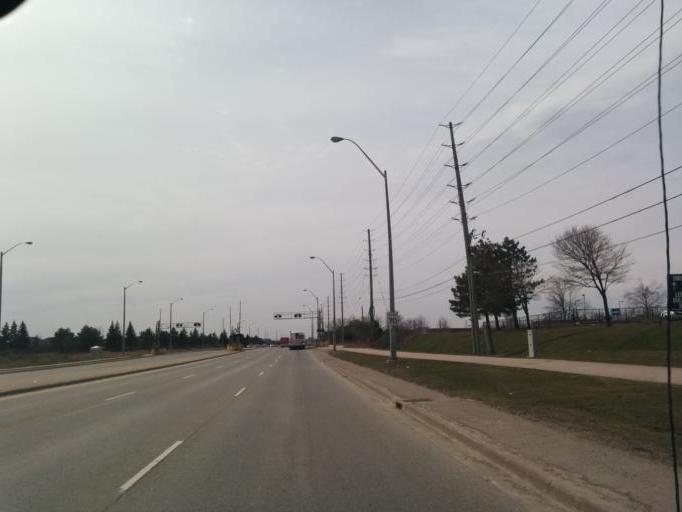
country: CA
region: Ontario
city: Brampton
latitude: 43.7019
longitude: -79.7912
